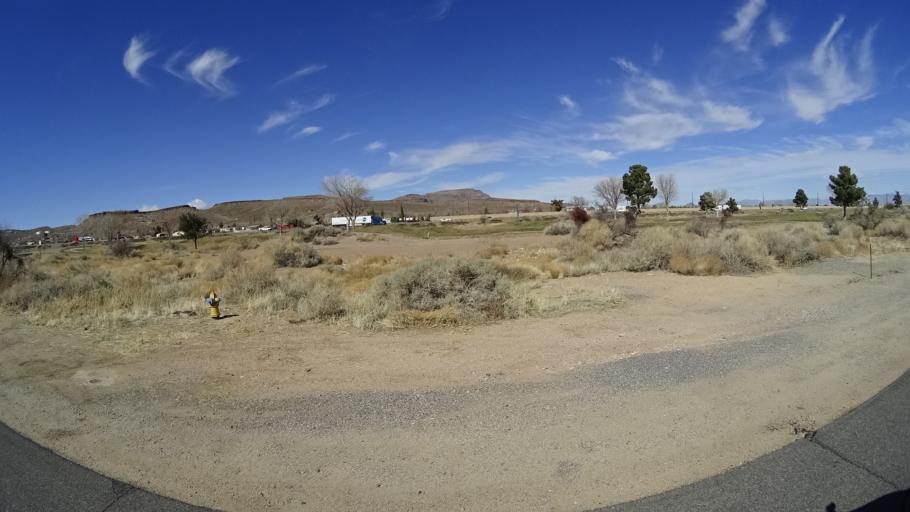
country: US
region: Arizona
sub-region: Mohave County
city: Kingman
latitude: 35.2124
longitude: -114.0481
